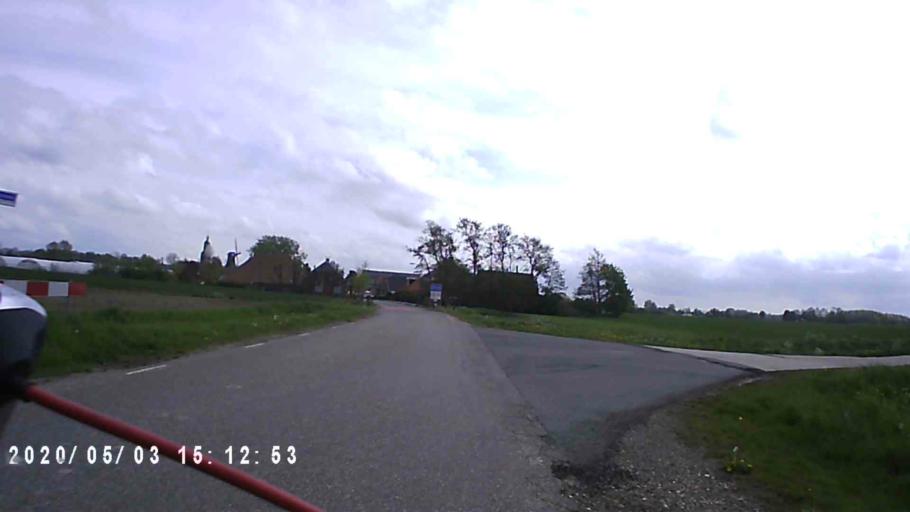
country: NL
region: Groningen
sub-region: Gemeente Winsum
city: Winsum
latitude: 53.3686
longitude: 6.4541
